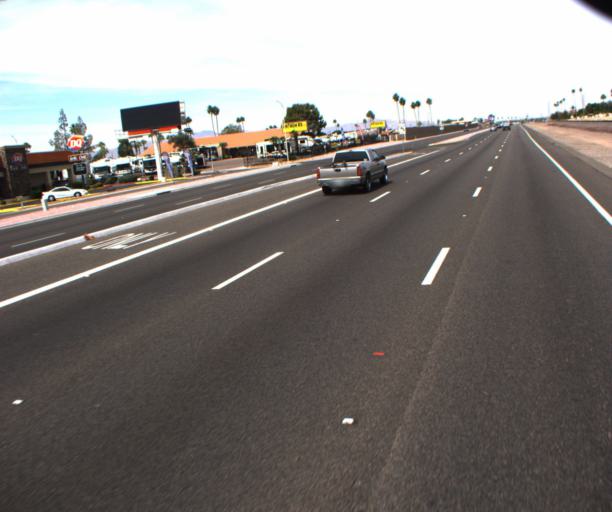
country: US
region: Arizona
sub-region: Maricopa County
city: Youngtown
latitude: 33.6036
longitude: -112.2927
